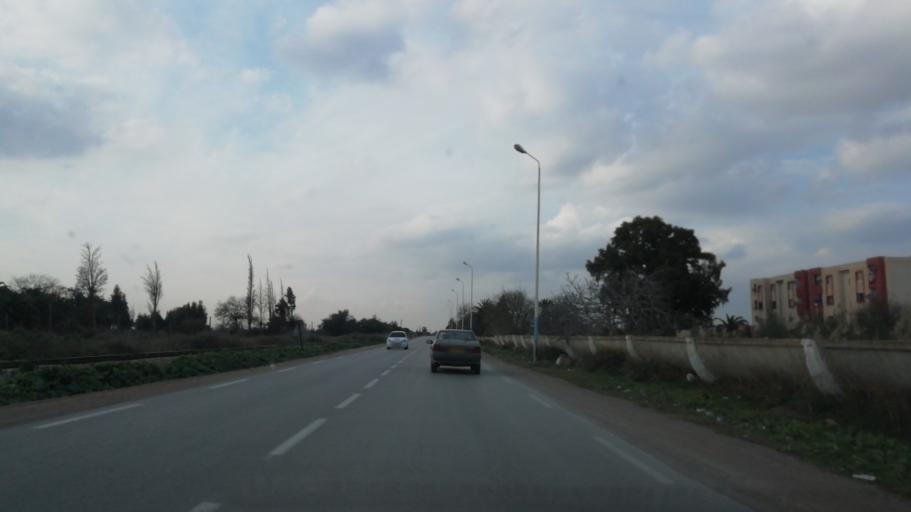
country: DZ
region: Mascara
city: Sig
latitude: 35.6567
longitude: 0.0139
